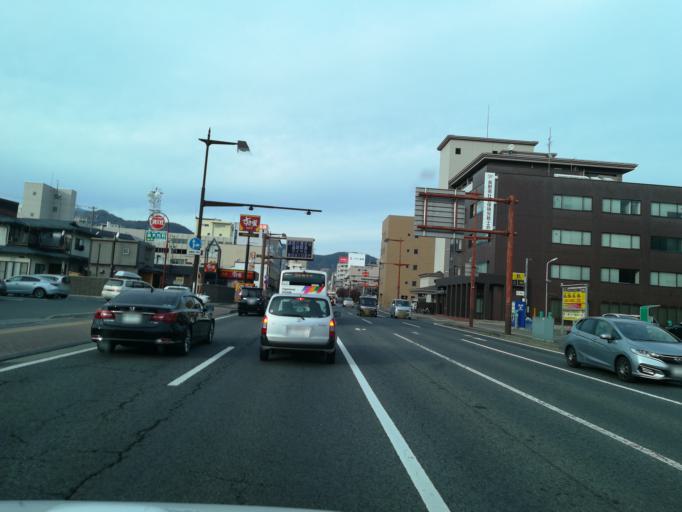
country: JP
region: Nagano
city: Nagano-shi
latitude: 36.6413
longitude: 138.1818
